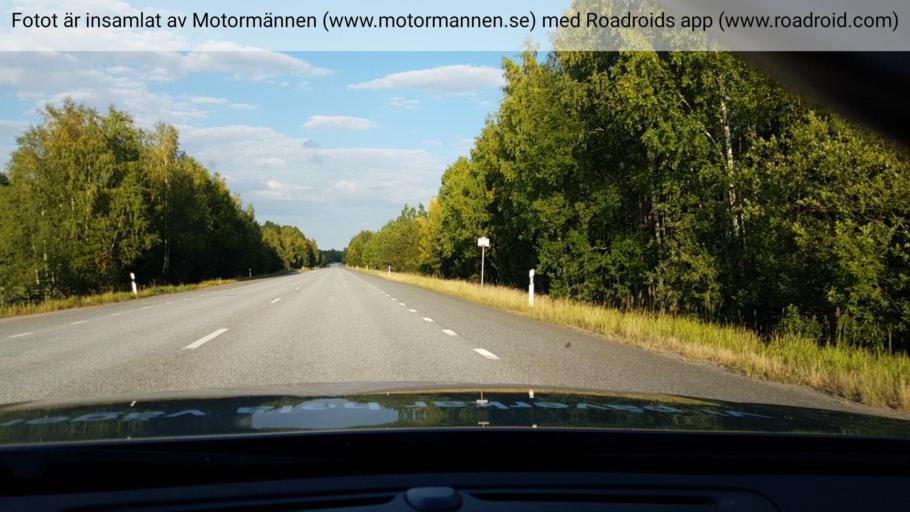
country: SE
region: Uppsala
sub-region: Heby Kommun
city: Morgongava
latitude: 59.8947
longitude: 17.1339
